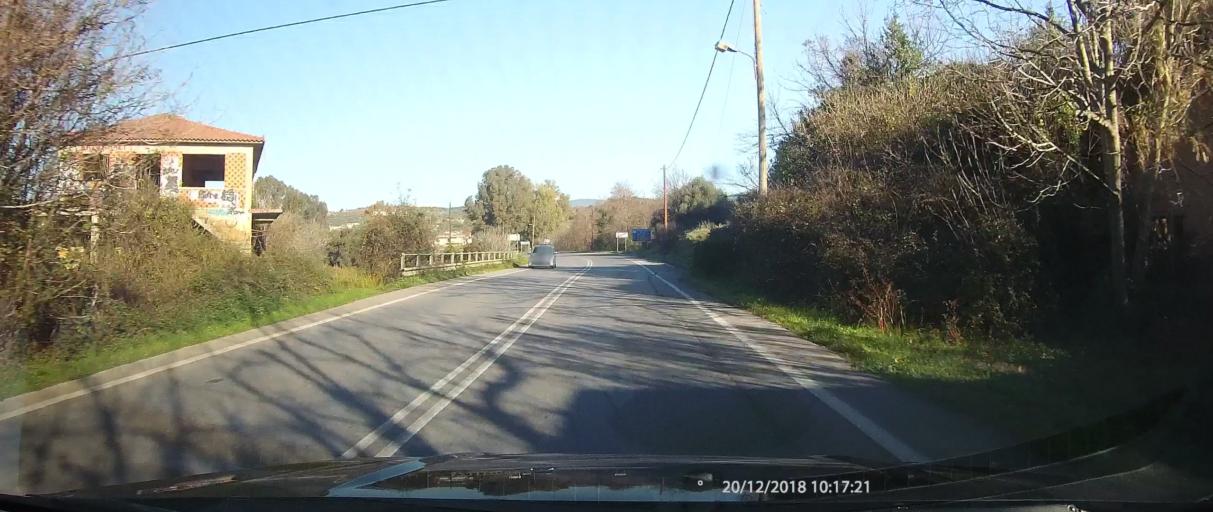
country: GR
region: Peloponnese
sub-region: Nomos Lakonias
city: Sparti
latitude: 37.1055
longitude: 22.4343
